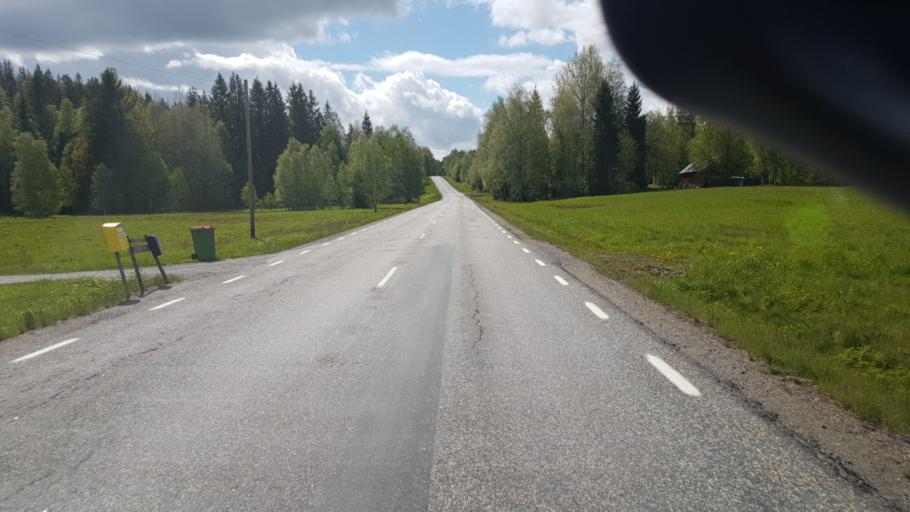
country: SE
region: Vaermland
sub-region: Arjangs Kommun
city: Arjaeng
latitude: 59.5788
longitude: 12.1236
